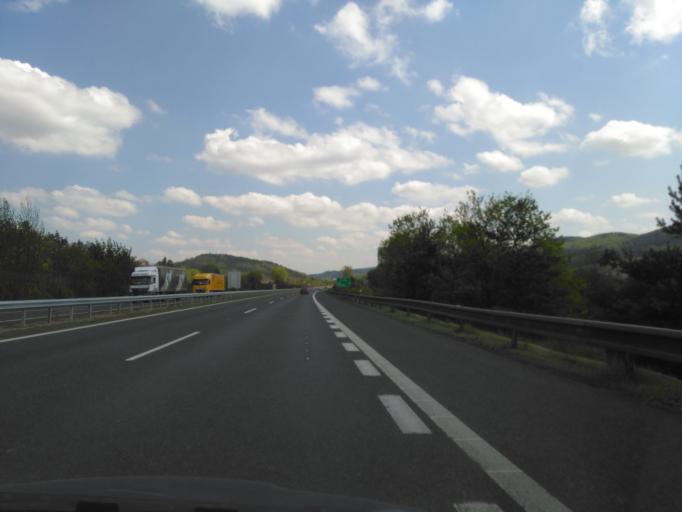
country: CZ
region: Central Bohemia
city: Zdice
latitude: 49.9043
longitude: 13.9667
